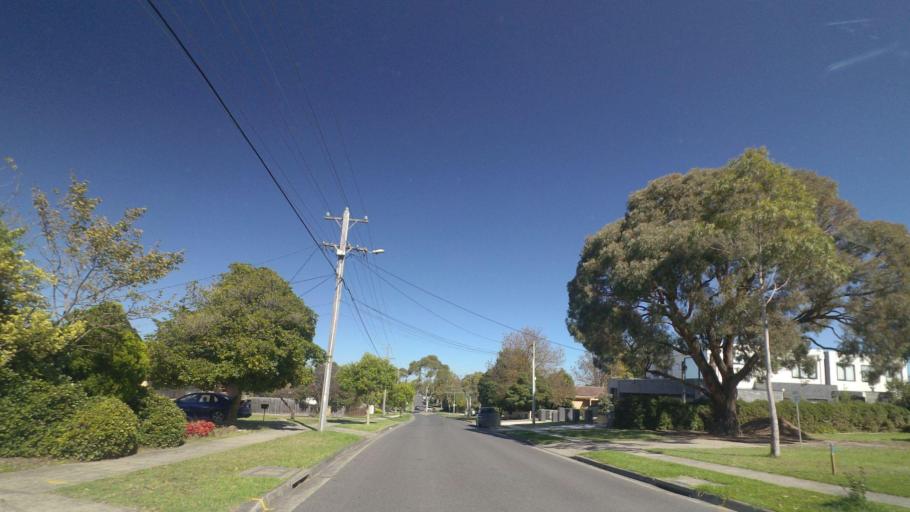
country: AU
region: Victoria
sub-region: Manningham
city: Donvale
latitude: -37.7937
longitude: 145.1703
